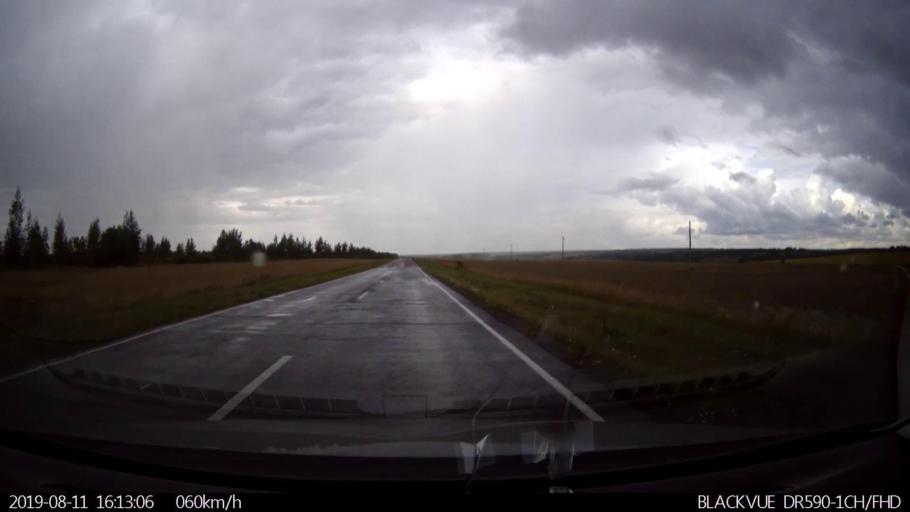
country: RU
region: Ulyanovsk
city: Ignatovka
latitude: 54.0173
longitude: 47.6381
